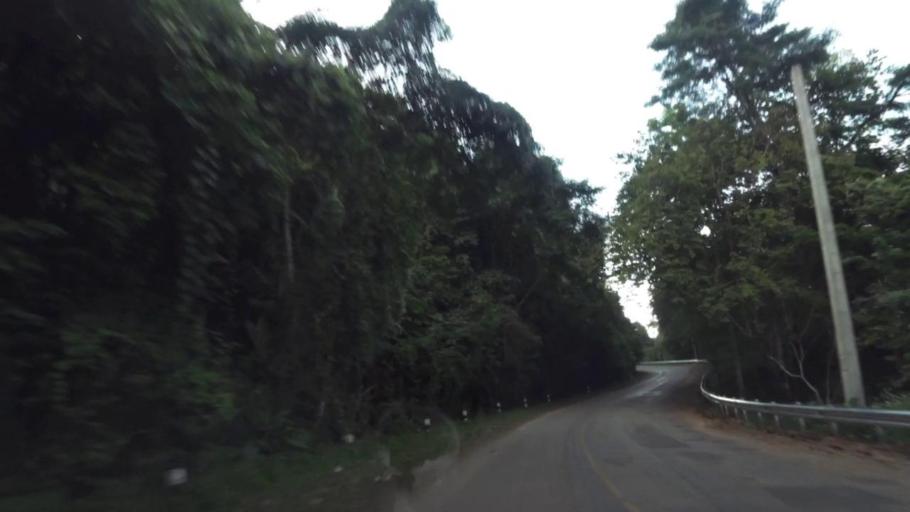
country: TH
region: Chiang Rai
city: Khun Tan
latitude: 19.8653
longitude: 100.4430
